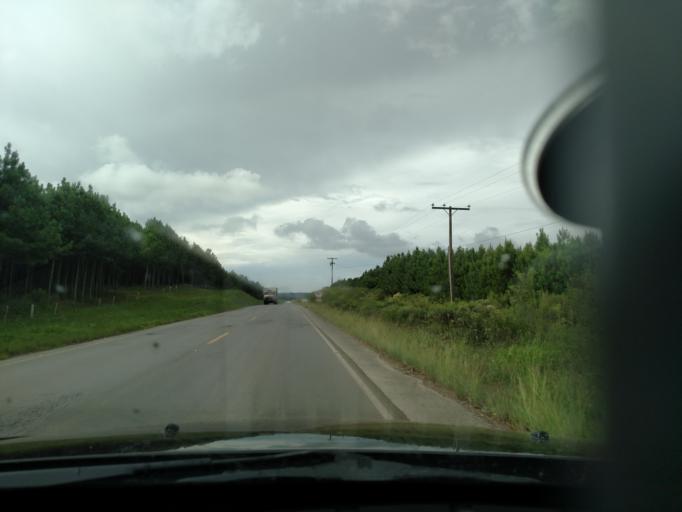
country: BR
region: Santa Catarina
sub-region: Lages
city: Lages
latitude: -27.7523
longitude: -50.1979
